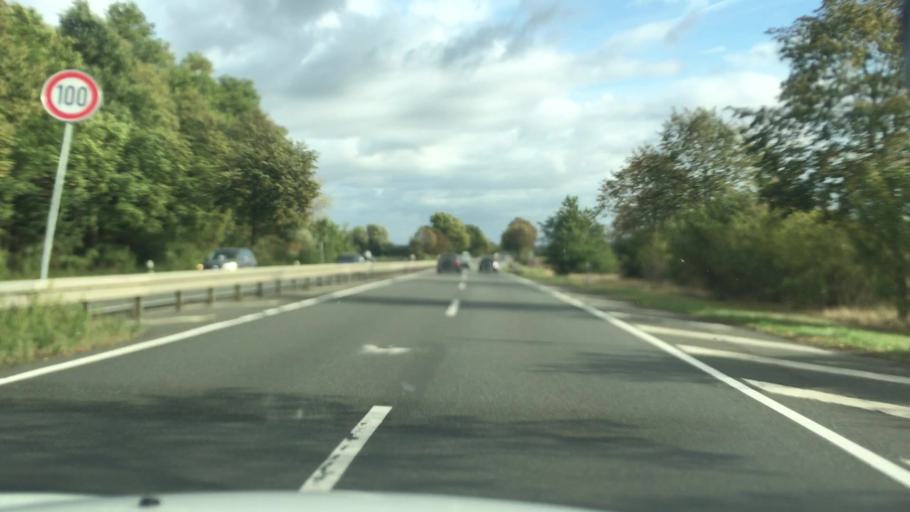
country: DE
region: Lower Saxony
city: Garbsen
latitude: 52.4541
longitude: 9.5516
